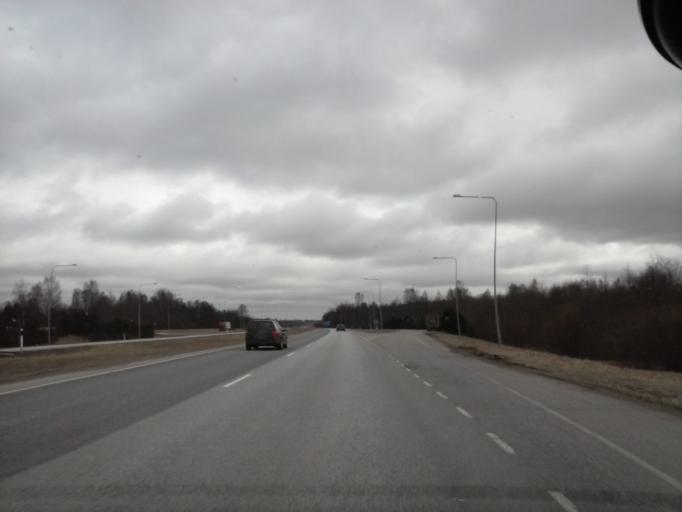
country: EE
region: Harju
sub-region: Rae vald
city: Vaida
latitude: 59.2999
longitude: 24.9500
